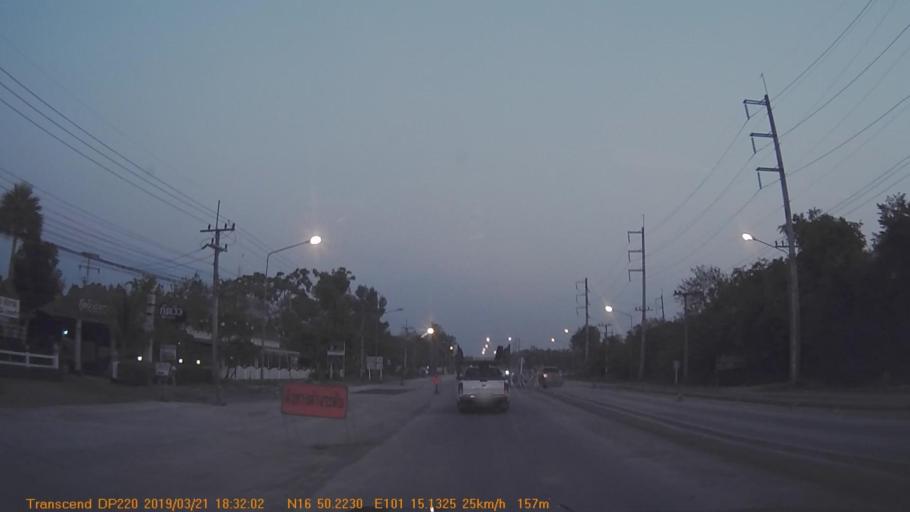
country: TH
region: Phetchabun
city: Lom Kao
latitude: 16.8369
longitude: 101.2522
